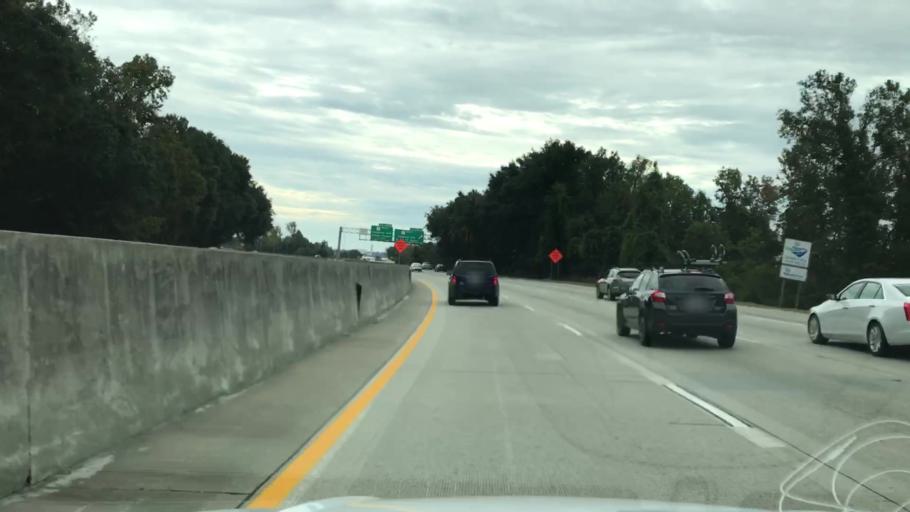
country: US
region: South Carolina
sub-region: Charleston County
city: North Charleston
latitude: 32.8462
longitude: -79.9862
